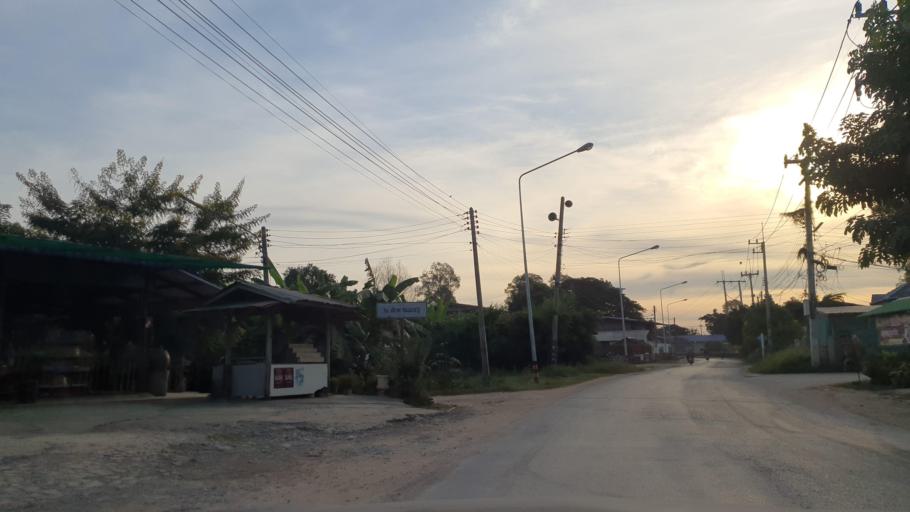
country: TH
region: Nakhon Sawan
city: Nakhon Sawan
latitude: 15.6634
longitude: 100.0570
